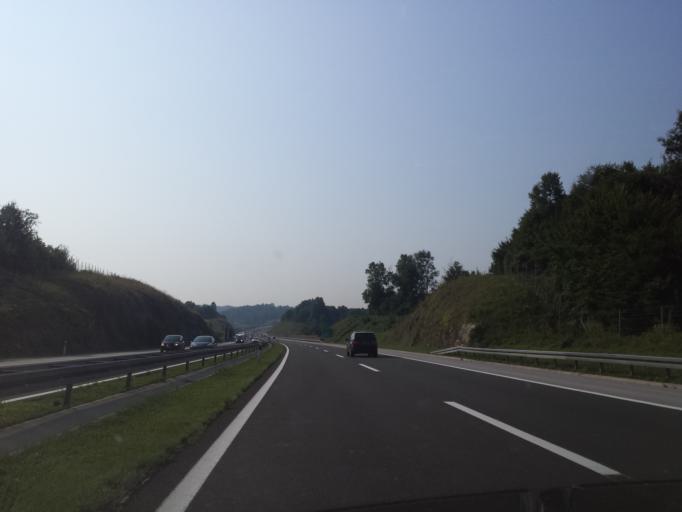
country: HR
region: Karlovacka
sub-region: Grad Ogulin
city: Ogulin
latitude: 45.3315
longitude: 15.2768
